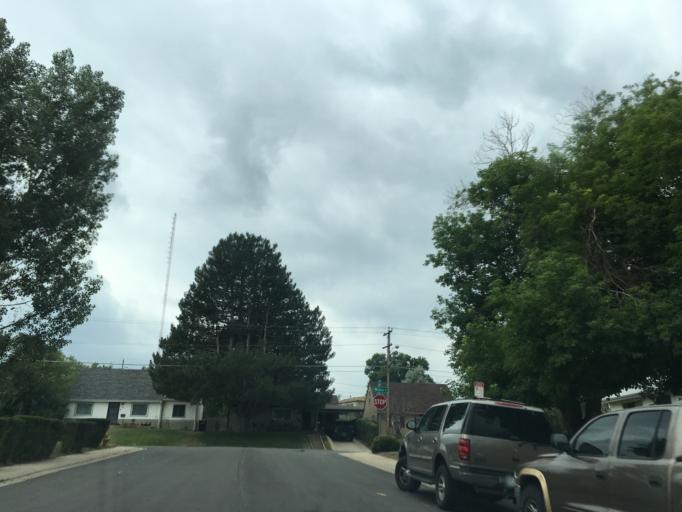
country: US
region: Colorado
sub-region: Arapahoe County
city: Sheridan
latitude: 39.6863
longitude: -105.0080
